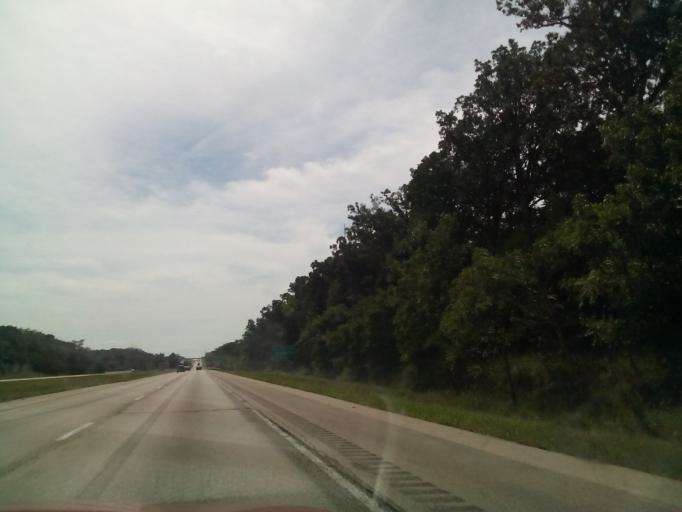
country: US
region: Illinois
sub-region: Winnebago County
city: Cherry Valley
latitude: 42.1874
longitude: -89.0242
